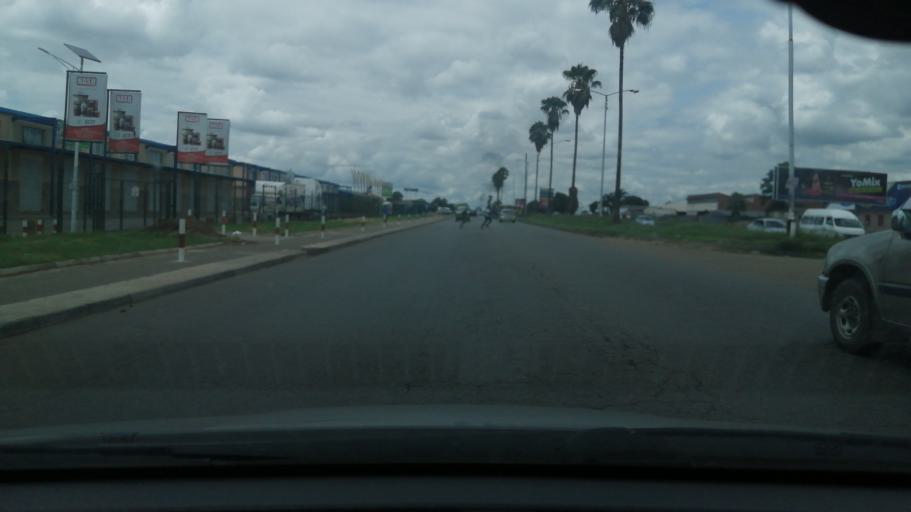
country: ZW
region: Harare
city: Harare
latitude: -17.8638
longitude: 31.0258
